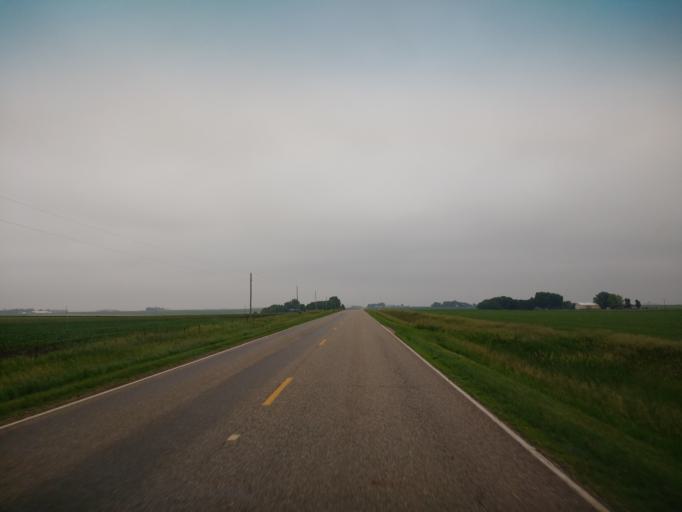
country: US
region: Iowa
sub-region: Sioux County
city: Alton
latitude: 42.9930
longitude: -95.8994
